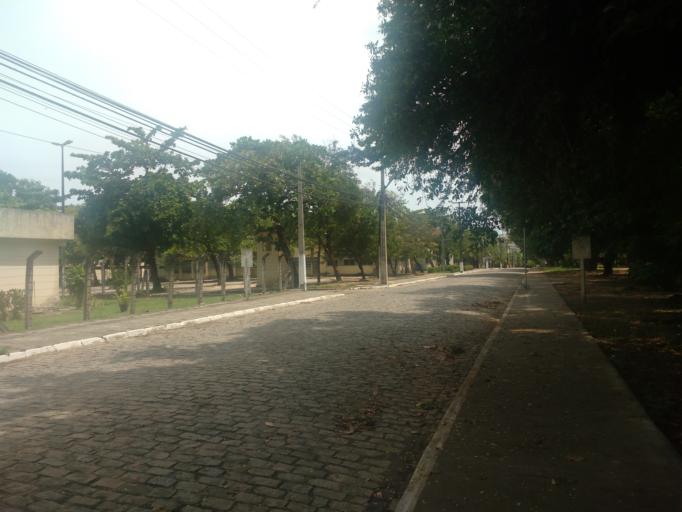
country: BR
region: Ceara
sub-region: Fortaleza
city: Fortaleza
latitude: -3.7455
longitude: -38.5774
